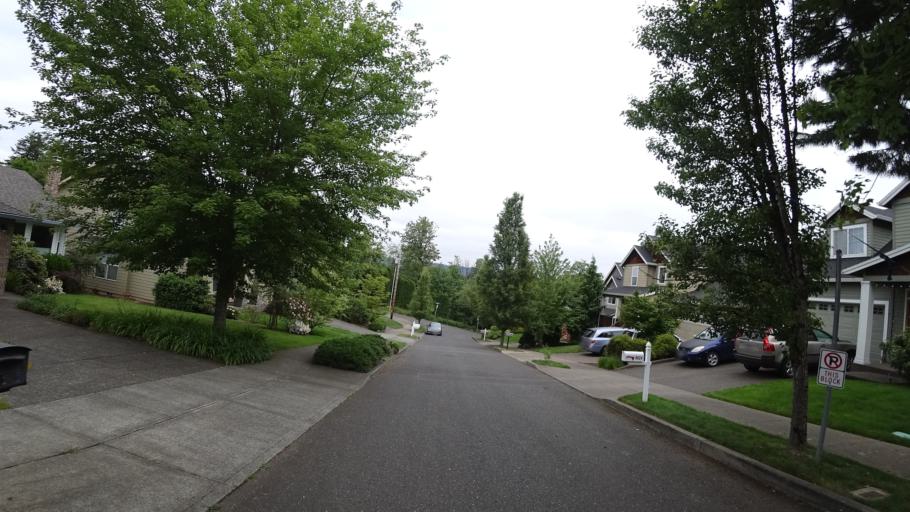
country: US
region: Oregon
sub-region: Washington County
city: Garden Home-Whitford
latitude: 45.4613
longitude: -122.7284
